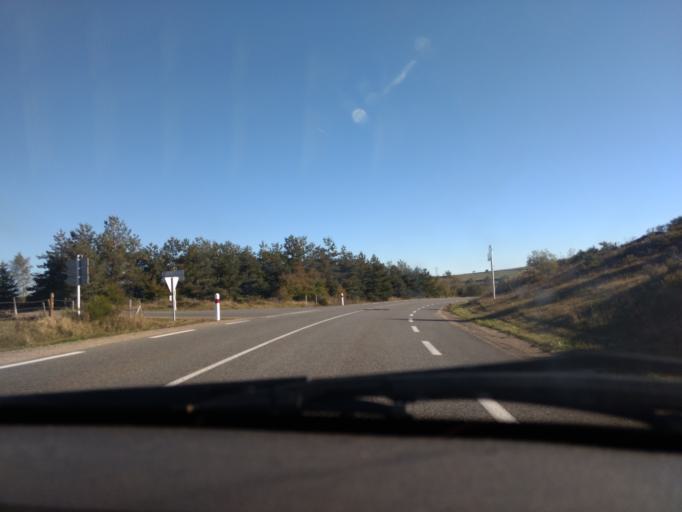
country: FR
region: Midi-Pyrenees
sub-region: Departement de l'Aveyron
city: Laguiole
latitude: 44.7552
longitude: 2.8743
